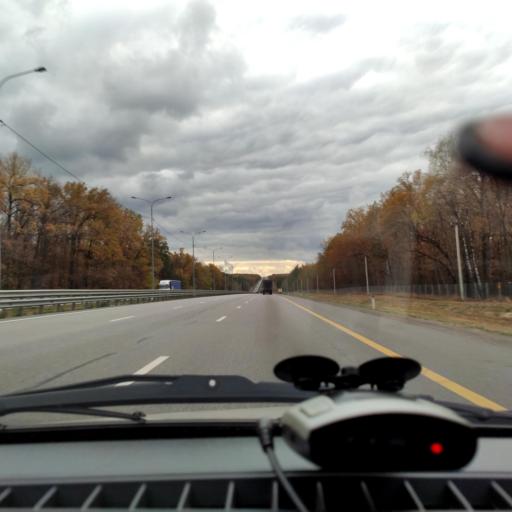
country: RU
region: Voronezj
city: Ramon'
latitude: 51.8779
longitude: 39.2169
